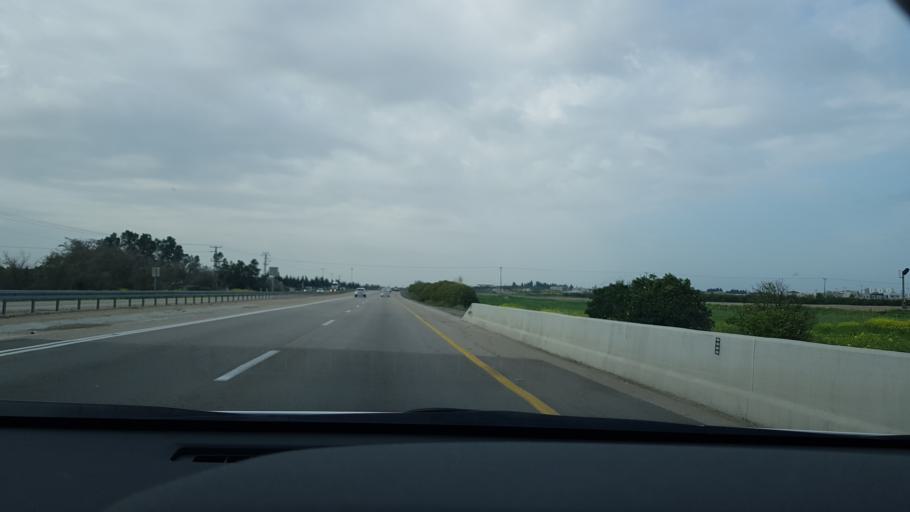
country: IL
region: Southern District
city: Ashqelon
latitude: 31.7048
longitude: 34.6216
